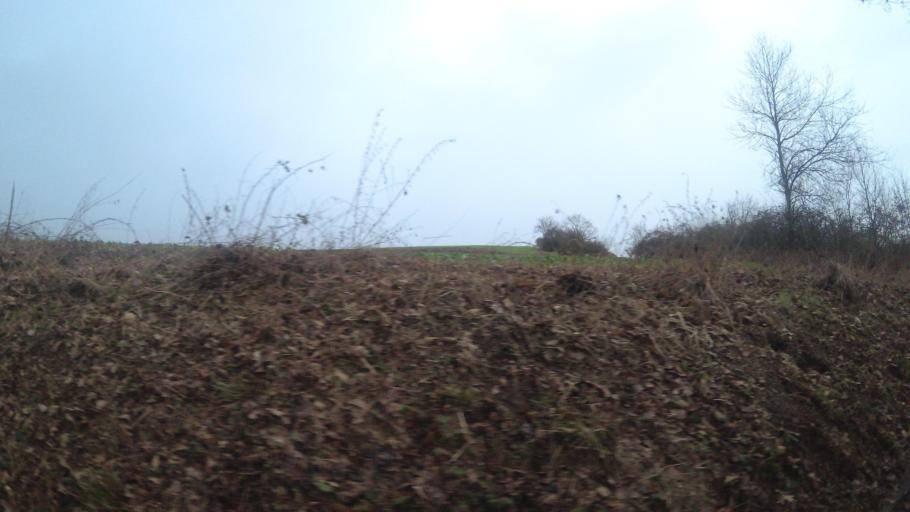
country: DE
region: Rheinland-Pfalz
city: Offenbach-Hundheim
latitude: 49.6142
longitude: 7.5355
